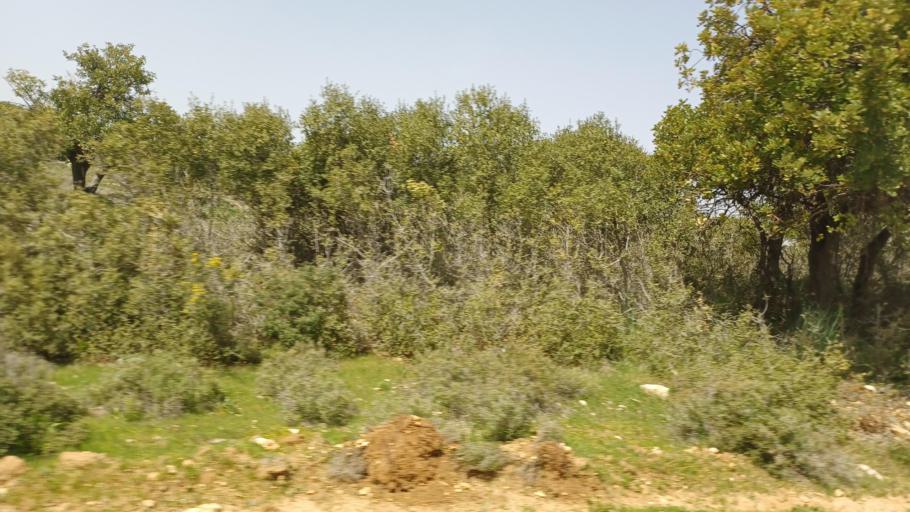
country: CY
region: Limassol
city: Pachna
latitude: 34.7524
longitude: 32.7468
